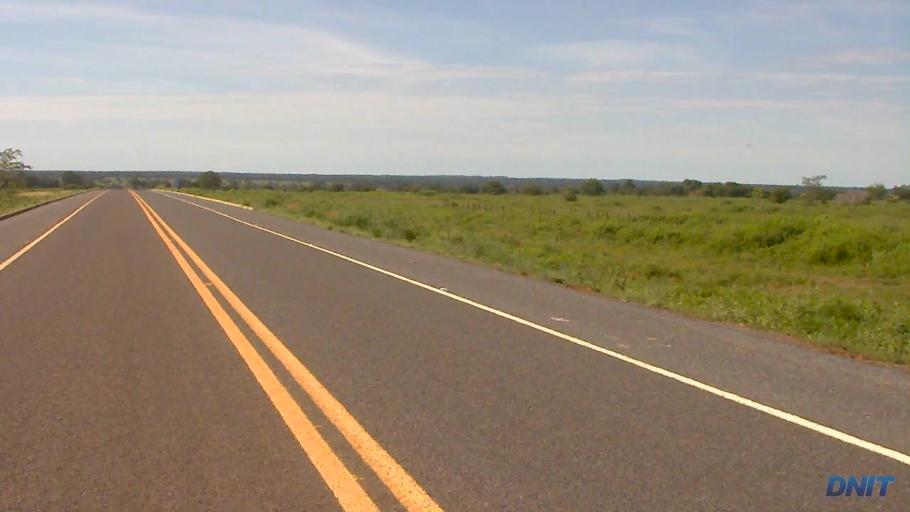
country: BR
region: Goias
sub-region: Sao Miguel Do Araguaia
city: Sao Miguel do Araguaia
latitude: -13.4837
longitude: -50.1111
